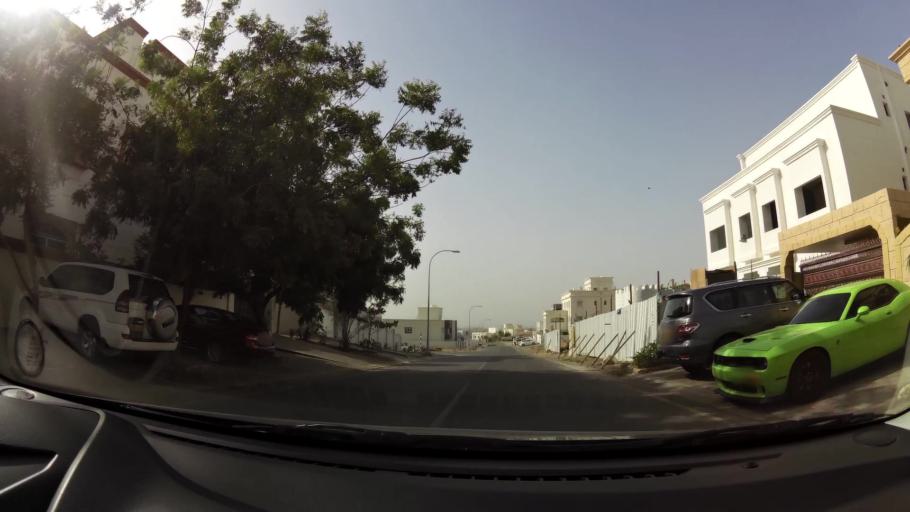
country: OM
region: Muhafazat Masqat
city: Bawshar
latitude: 23.5546
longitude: 58.3524
